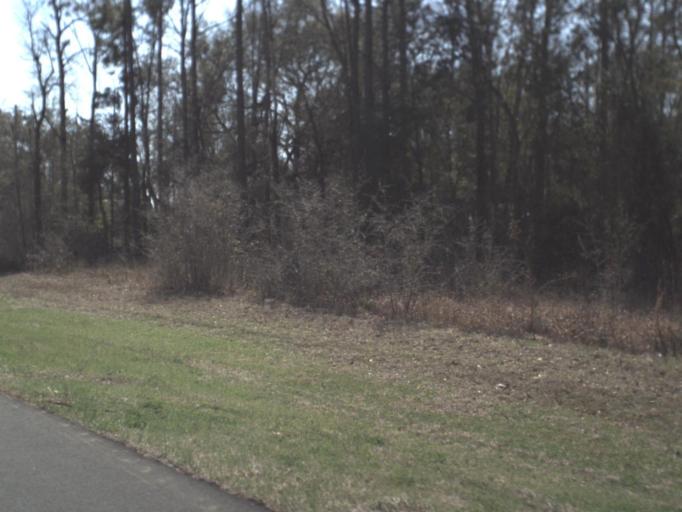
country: US
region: Florida
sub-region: Jackson County
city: Malone
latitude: 30.8410
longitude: -85.0646
